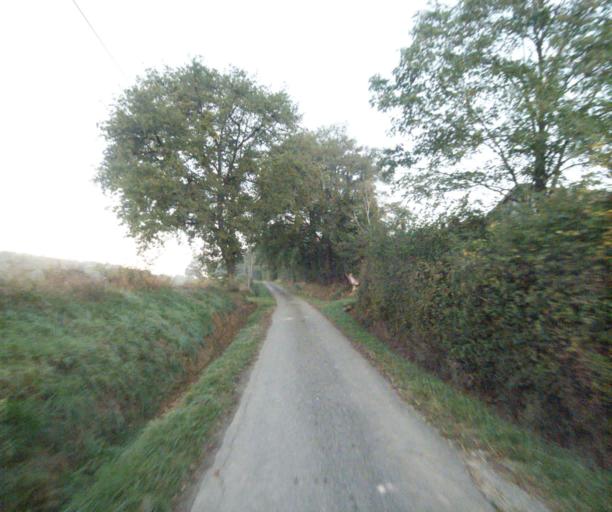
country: FR
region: Midi-Pyrenees
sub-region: Departement du Gers
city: Vic-Fezensac
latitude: 43.7759
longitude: 0.2320
